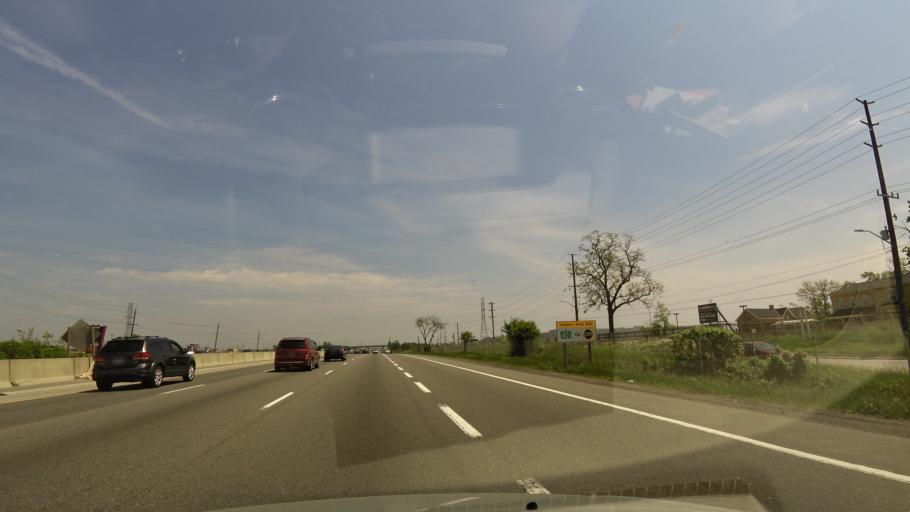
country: CA
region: Ontario
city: Oshawa
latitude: 43.8668
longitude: -78.9149
